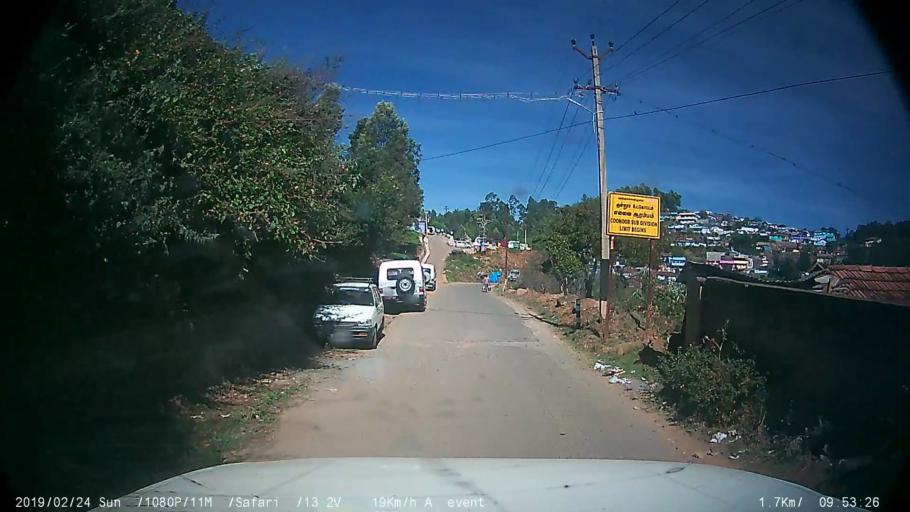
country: IN
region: Tamil Nadu
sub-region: Nilgiri
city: Wellington
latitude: 11.3548
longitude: 76.7729
